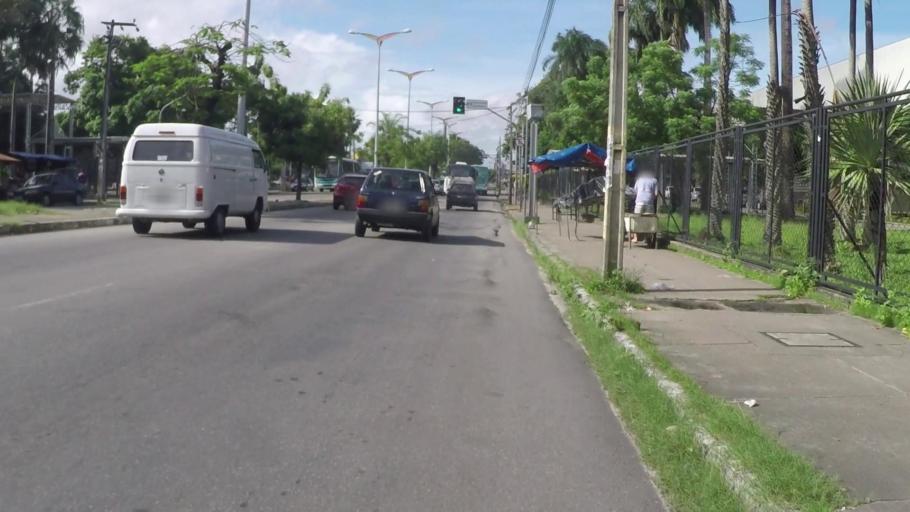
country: BR
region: Ceara
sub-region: Fortaleza
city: Fortaleza
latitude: -3.7325
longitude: -38.5846
